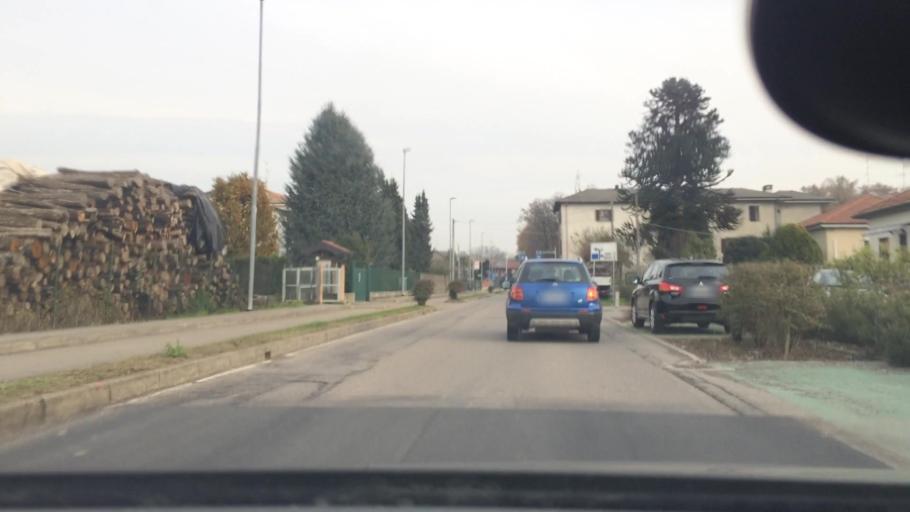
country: IT
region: Lombardy
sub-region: Provincia di Monza e Brianza
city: Misinto
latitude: 45.6649
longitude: 9.0773
